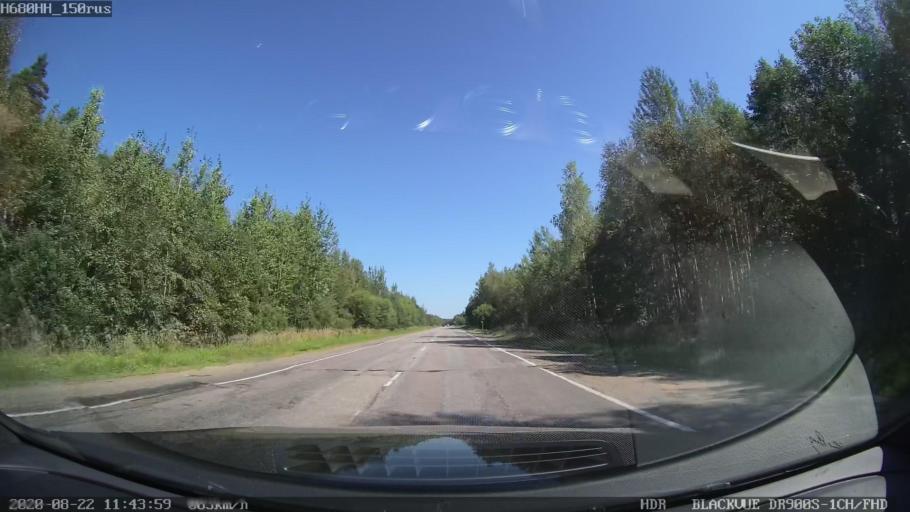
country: RU
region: Tverskaya
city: Sakharovo
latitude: 57.0168
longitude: 36.0420
